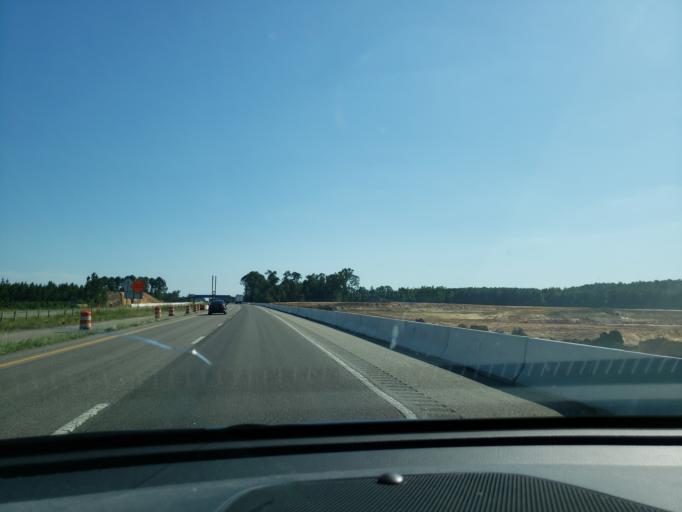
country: US
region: North Carolina
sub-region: Cumberland County
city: Hope Mills
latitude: 34.9055
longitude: -78.9573
